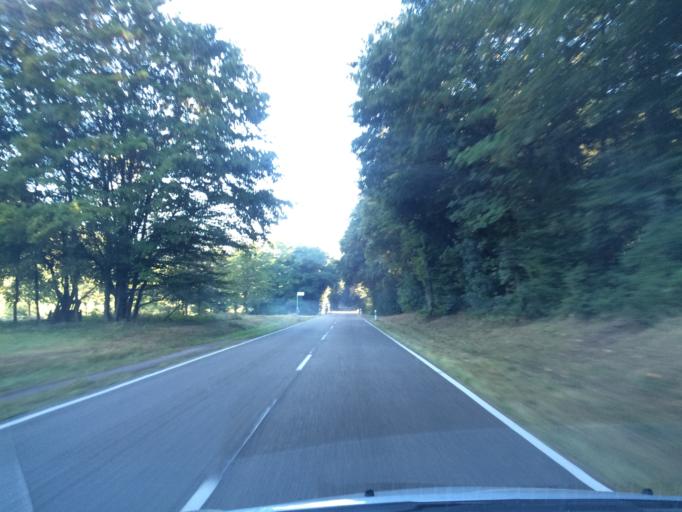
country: DE
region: Rheinland-Pfalz
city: Bobenthal
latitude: 49.0757
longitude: 7.8603
